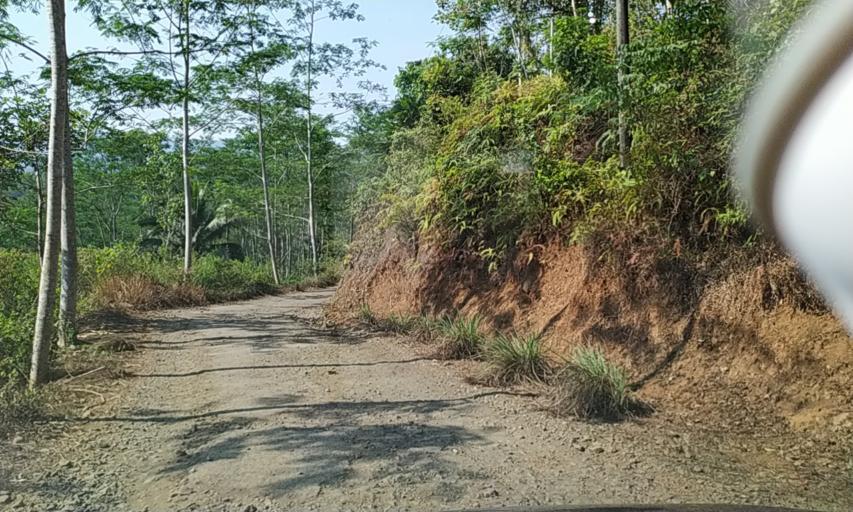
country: ID
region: Central Java
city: Datar
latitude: -7.2161
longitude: 108.6268
